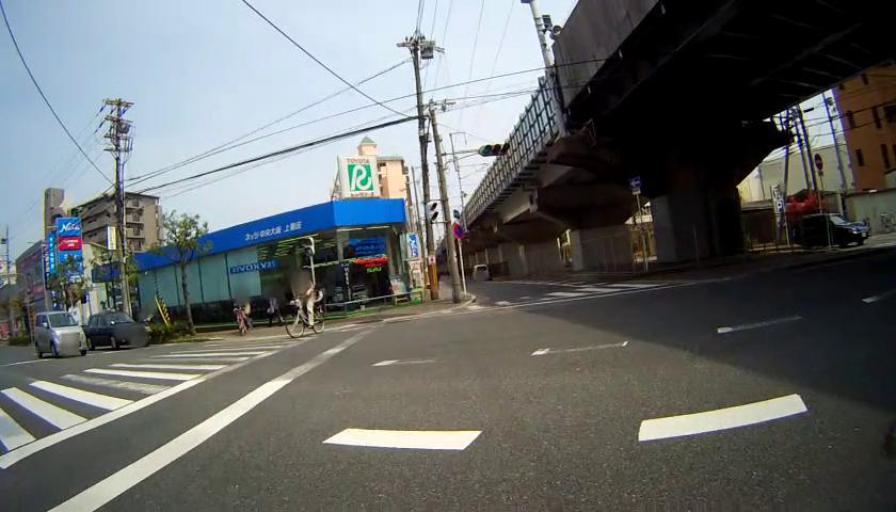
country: JP
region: Osaka
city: Suita
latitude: 34.7462
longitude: 135.5268
